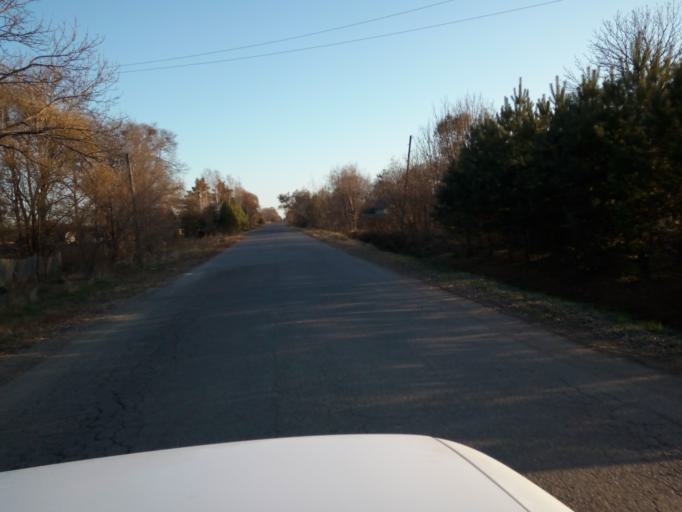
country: RU
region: Primorskiy
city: Lazo
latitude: 45.8659
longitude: 133.6434
